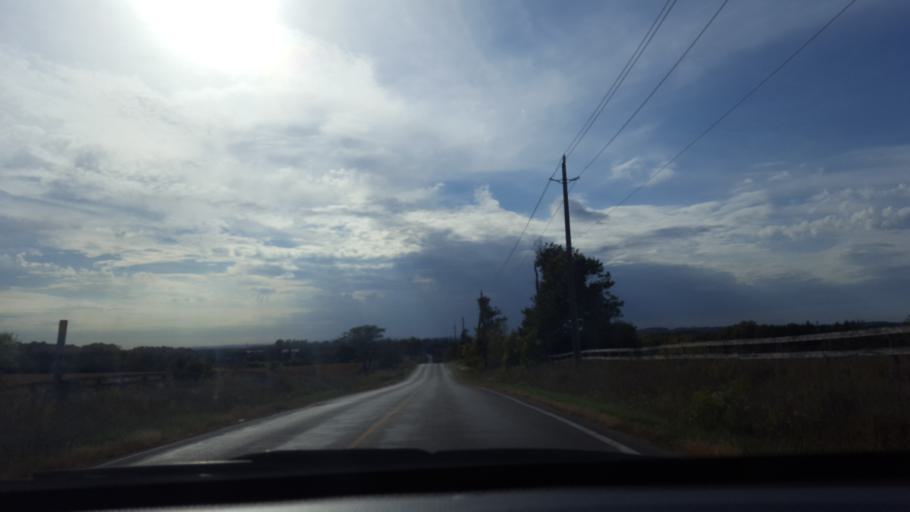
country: CA
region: Ontario
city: Vaughan
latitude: 43.8938
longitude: -79.6027
